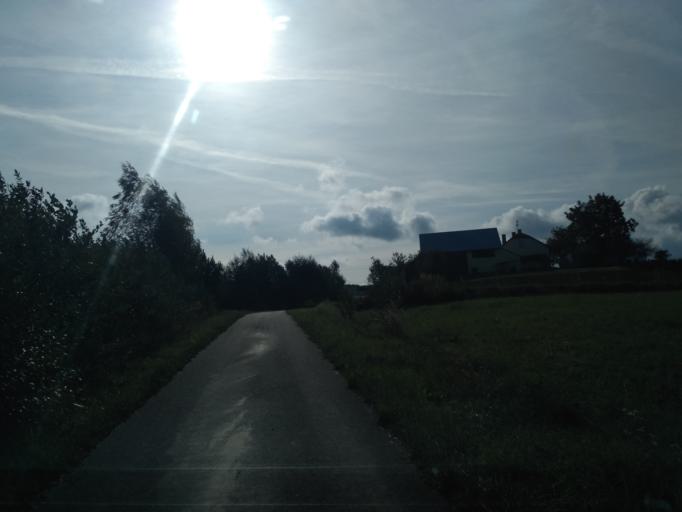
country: PL
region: Subcarpathian Voivodeship
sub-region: Powiat strzyzowski
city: Strzyzow
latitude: 49.8494
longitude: 21.8296
